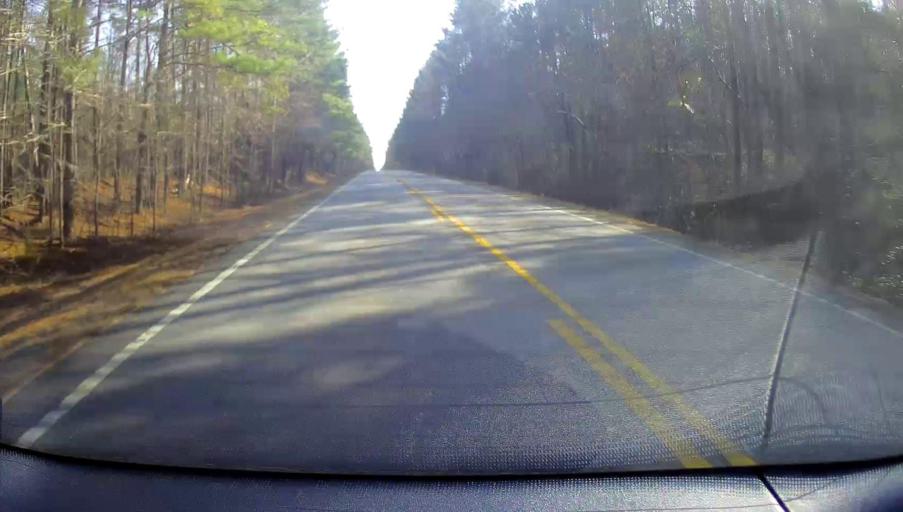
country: US
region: Georgia
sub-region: Butts County
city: Indian Springs
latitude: 33.1610
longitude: -83.8409
